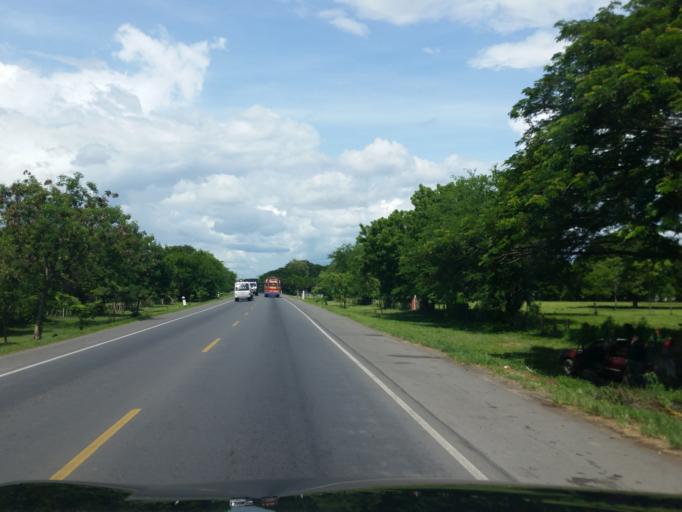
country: NI
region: Managua
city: Tipitapa
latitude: 12.1659
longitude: -86.1238
